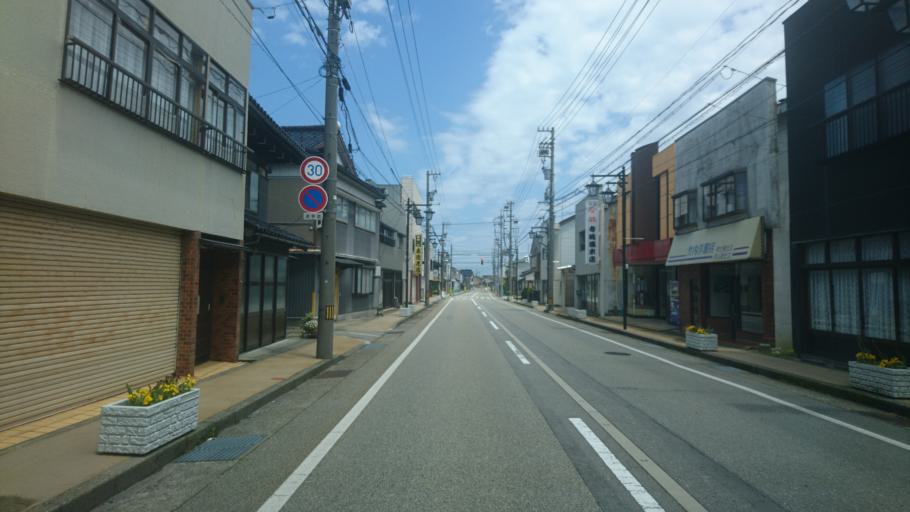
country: JP
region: Toyama
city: Nyuzen
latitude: 36.9412
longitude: 137.5029
